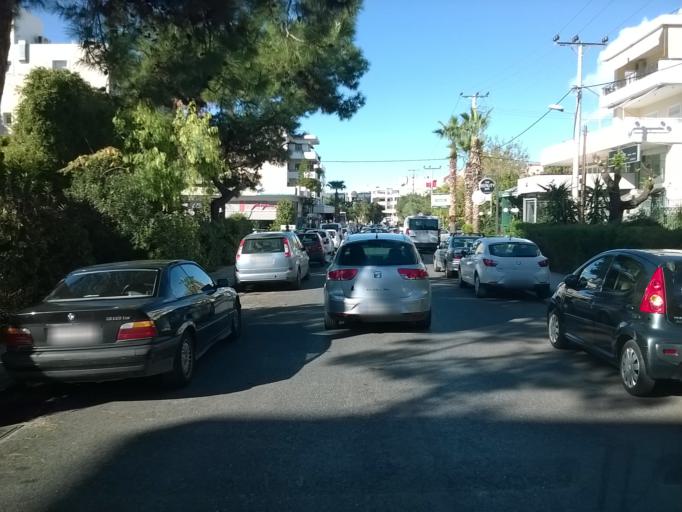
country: GR
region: Attica
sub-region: Nomarchia Athinas
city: Glyfada
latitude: 37.8615
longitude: 23.7569
